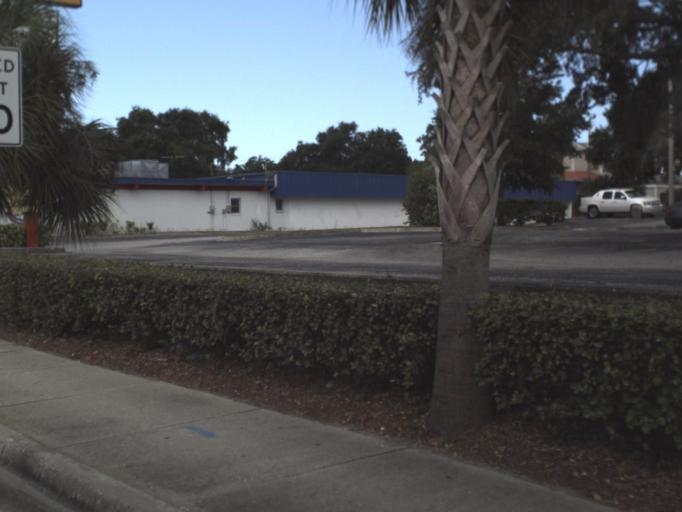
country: US
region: Florida
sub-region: Pinellas County
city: Seminole
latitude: 27.8413
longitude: -82.7872
